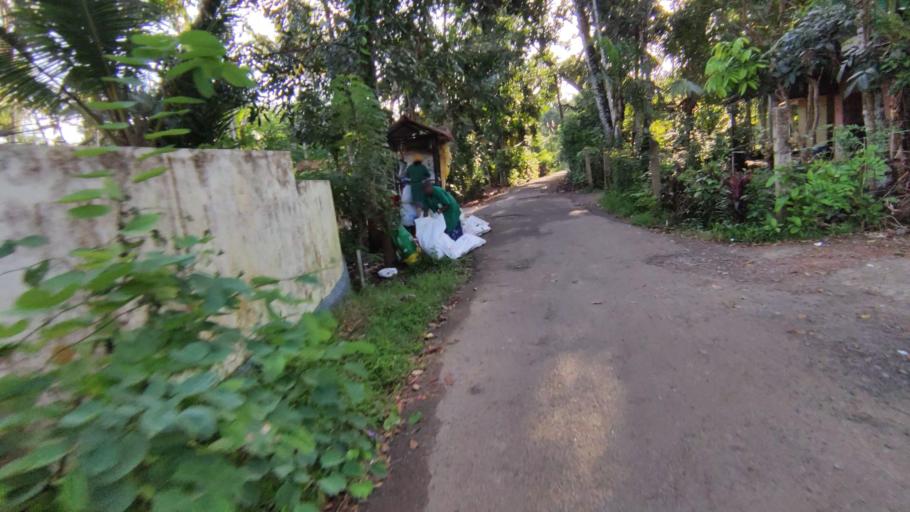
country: IN
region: Kerala
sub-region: Kottayam
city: Kottayam
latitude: 9.5975
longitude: 76.4852
